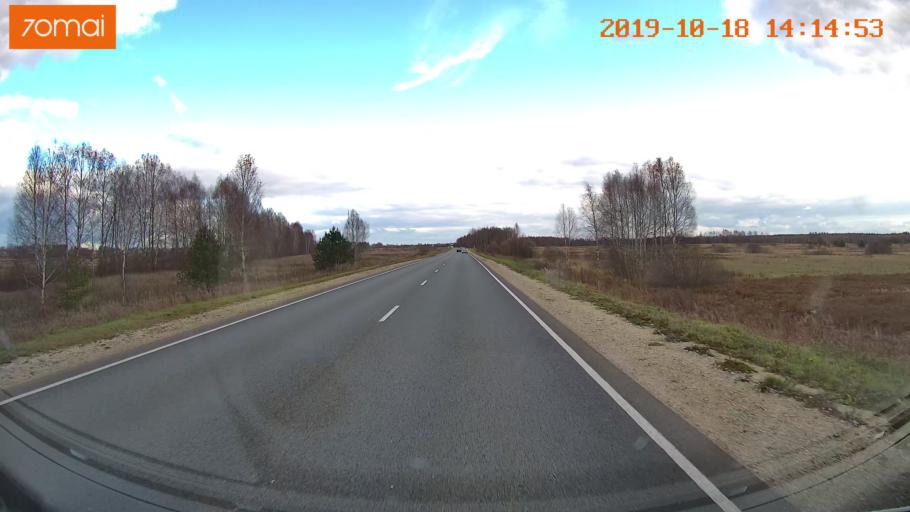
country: RU
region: Rjazan
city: Spas-Klepiki
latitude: 55.1480
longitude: 40.3050
